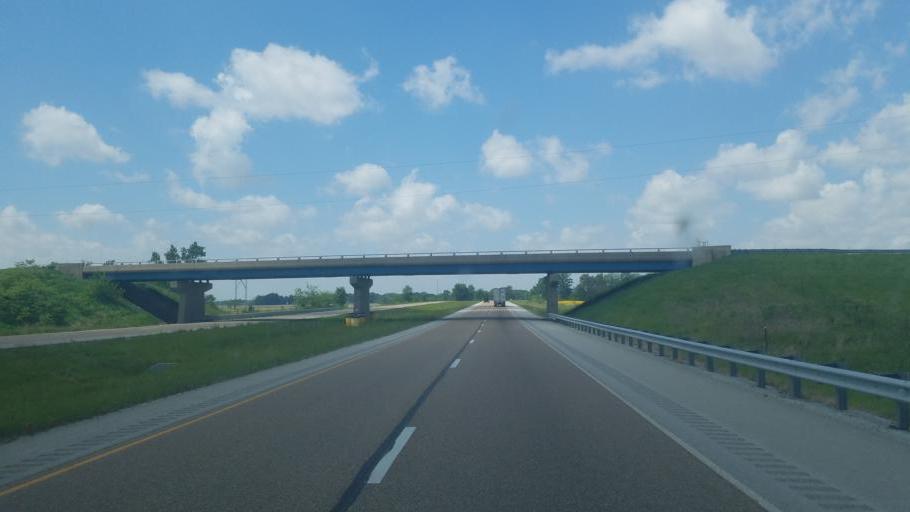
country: US
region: Illinois
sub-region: Cumberland County
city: Greenup
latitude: 39.2796
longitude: -88.0803
